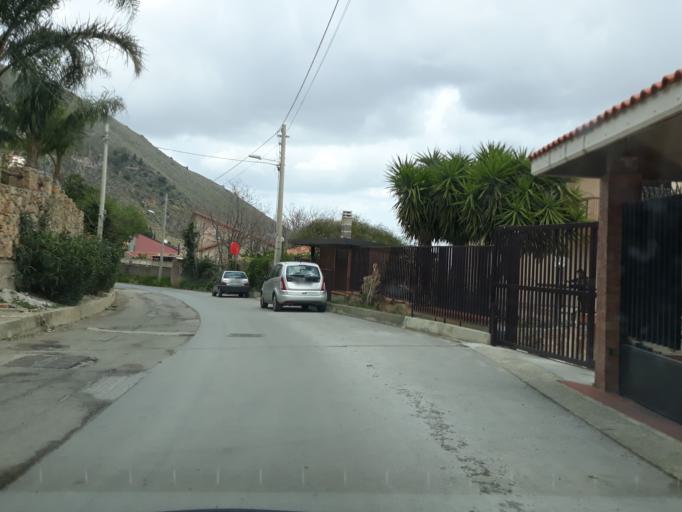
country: IT
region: Sicily
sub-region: Palermo
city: Monreale
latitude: 38.0825
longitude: 13.2977
